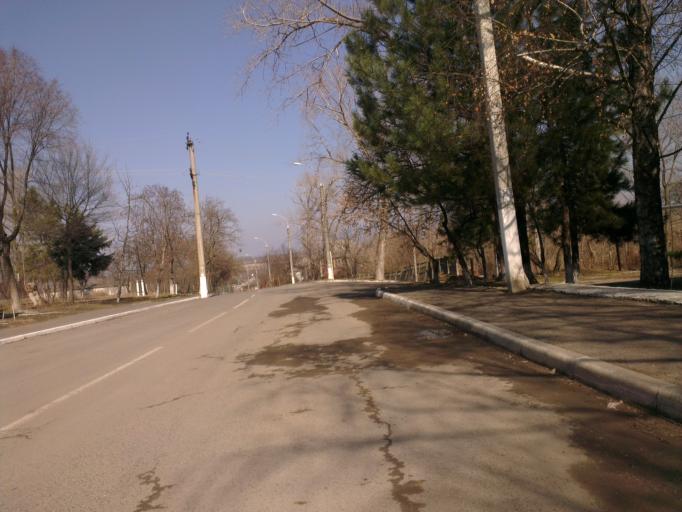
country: MD
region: Chisinau
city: Cricova
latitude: 47.1431
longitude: 28.8639
